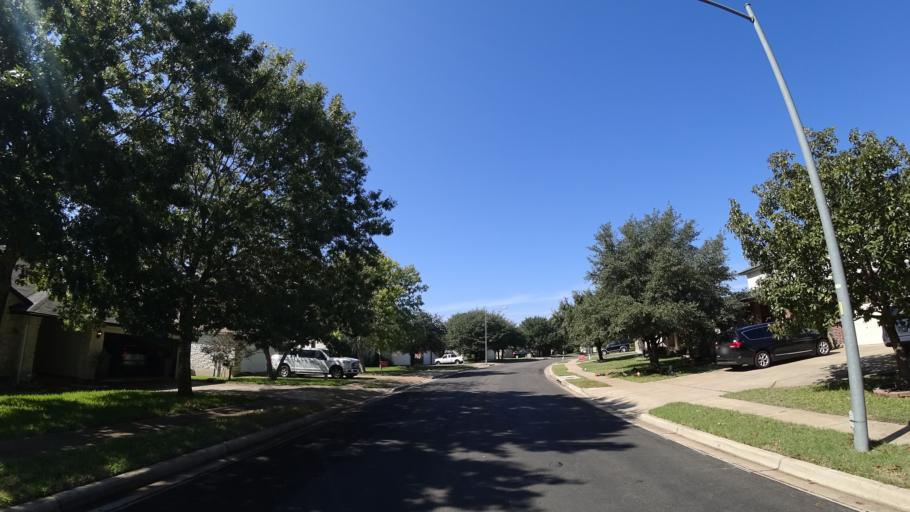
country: US
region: Texas
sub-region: Travis County
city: Shady Hollow
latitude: 30.1935
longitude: -97.8626
